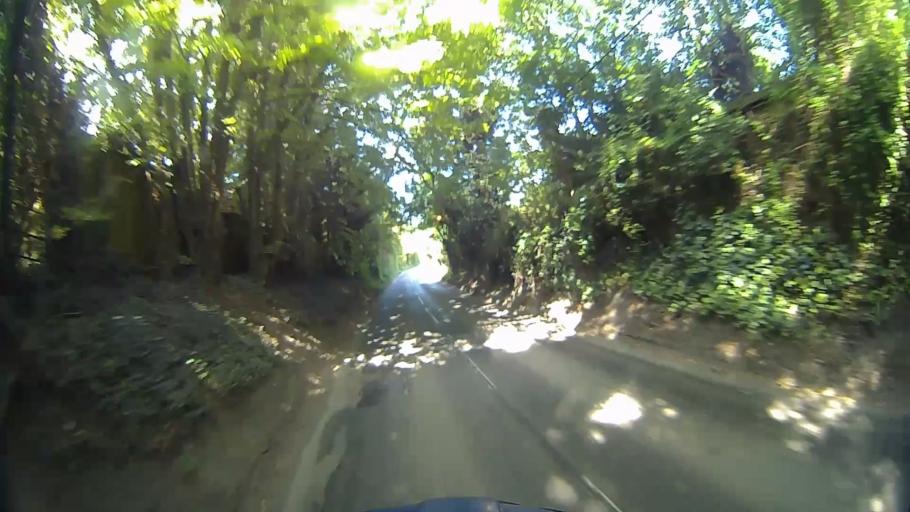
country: GB
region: England
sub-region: Oxfordshire
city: Wantage
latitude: 51.5862
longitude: -1.4319
